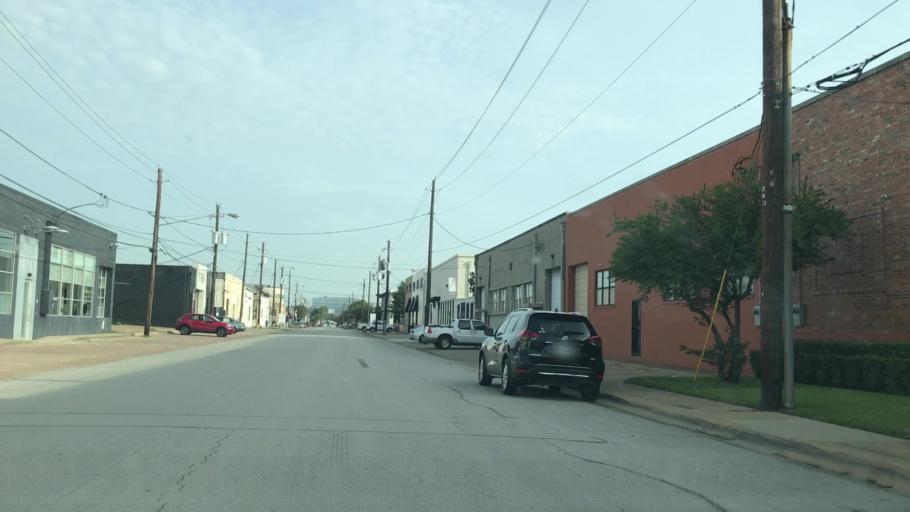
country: US
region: Texas
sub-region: Dallas County
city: Dallas
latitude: 32.7870
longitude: -96.8165
